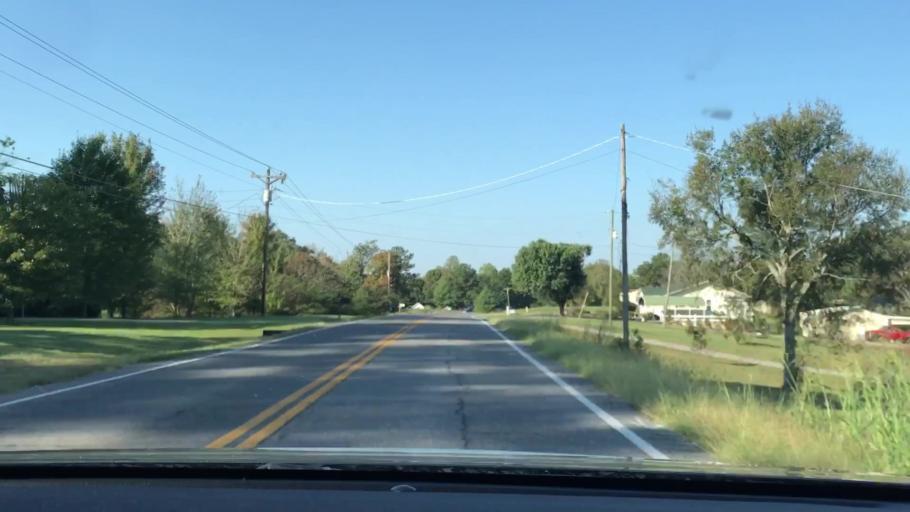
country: US
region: Kentucky
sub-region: Marshall County
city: Benton
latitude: 36.7678
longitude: -88.1798
